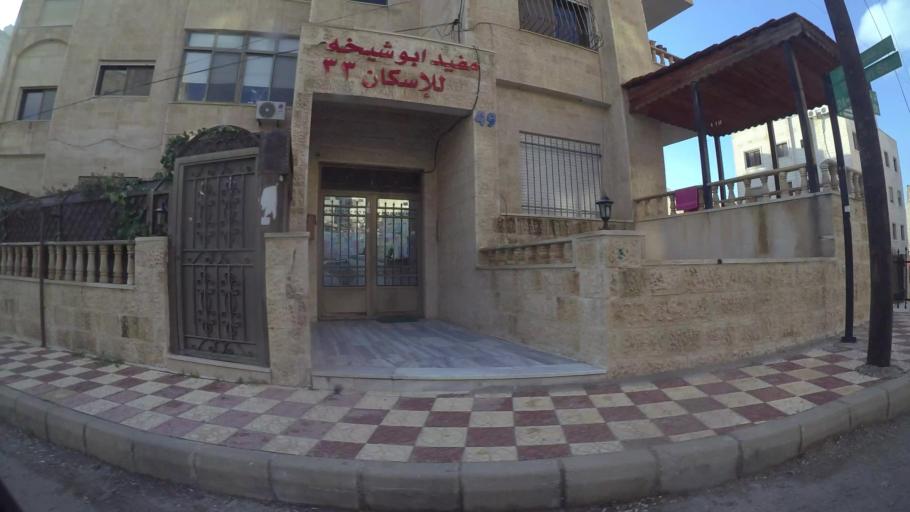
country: JO
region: Amman
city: Al Jubayhah
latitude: 31.9985
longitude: 35.8675
